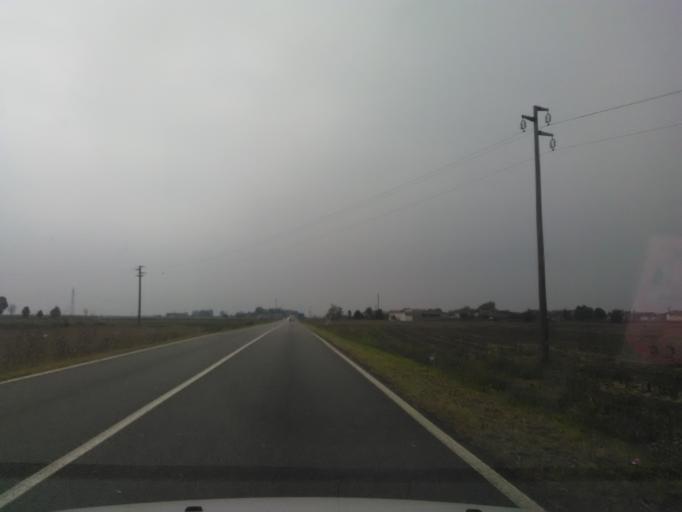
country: IT
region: Piedmont
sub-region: Provincia di Vercelli
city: Livorno Ferraris
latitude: 45.2853
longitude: 8.0927
